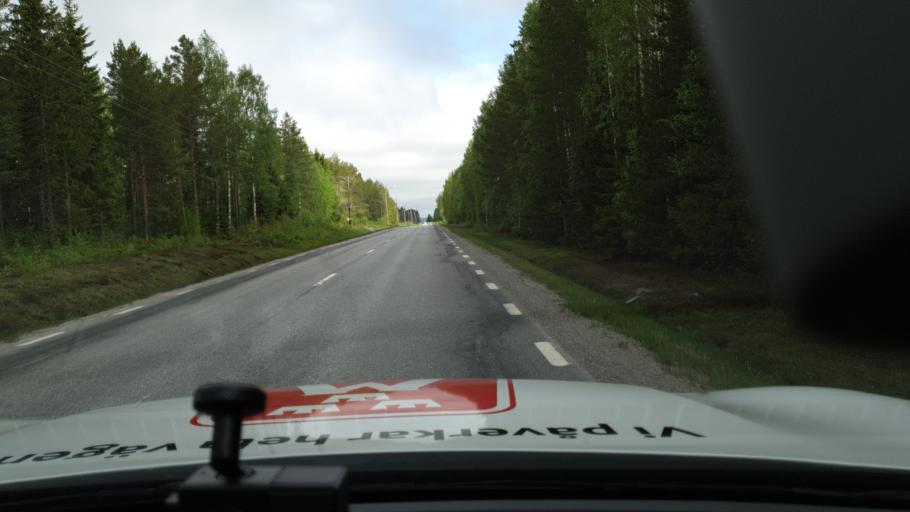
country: SE
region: Vaesterbotten
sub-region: Umea Kommun
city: Roback
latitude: 63.9027
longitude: 20.1984
